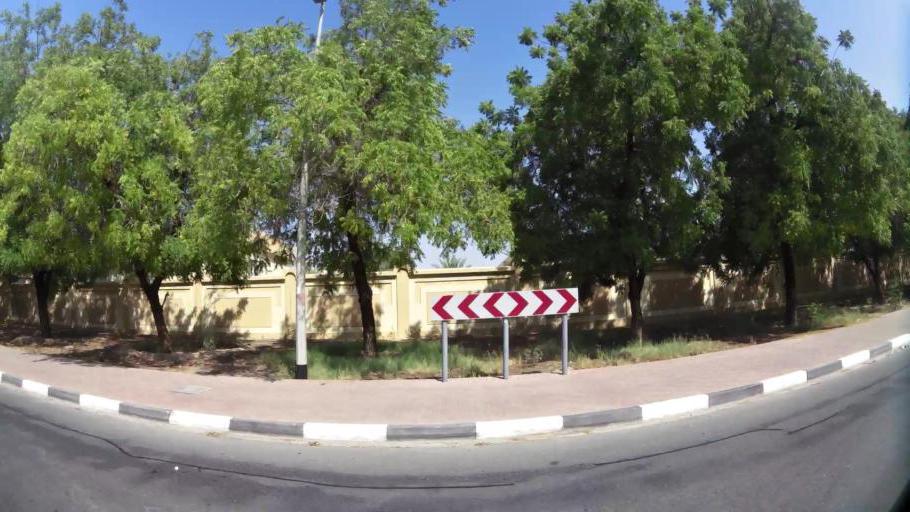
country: AE
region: Ash Shariqah
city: Sharjah
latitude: 25.2650
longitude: 55.3712
